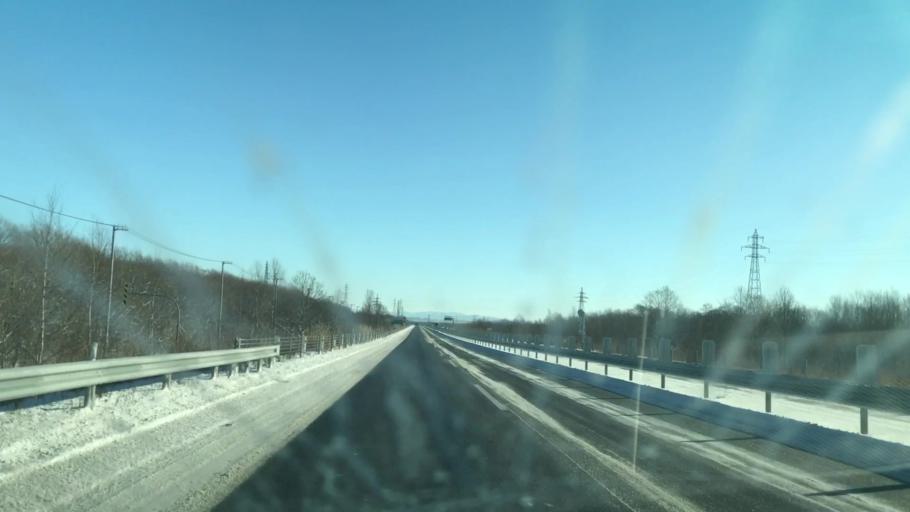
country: JP
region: Hokkaido
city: Tomakomai
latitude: 42.6736
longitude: 141.7542
